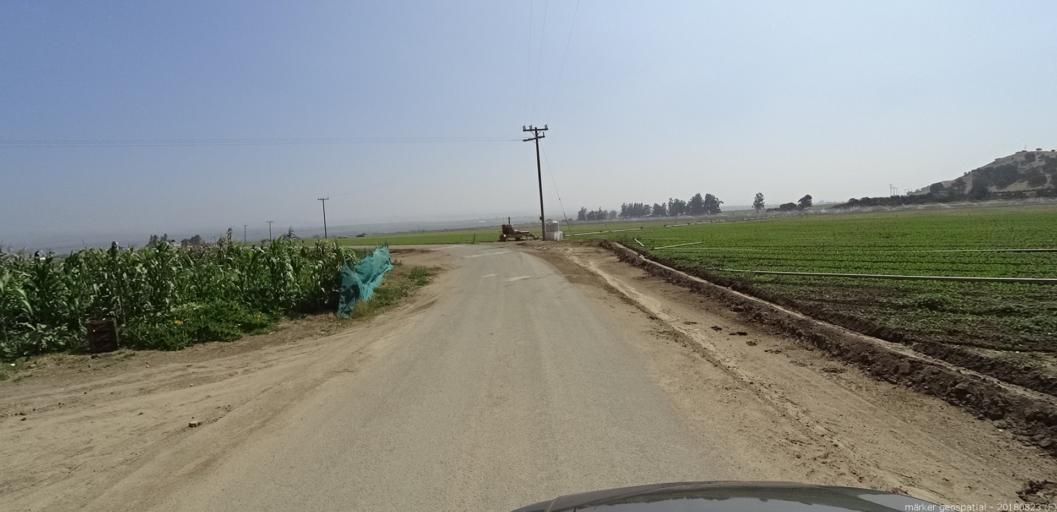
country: US
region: California
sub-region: Monterey County
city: King City
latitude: 36.2272
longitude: -121.1850
